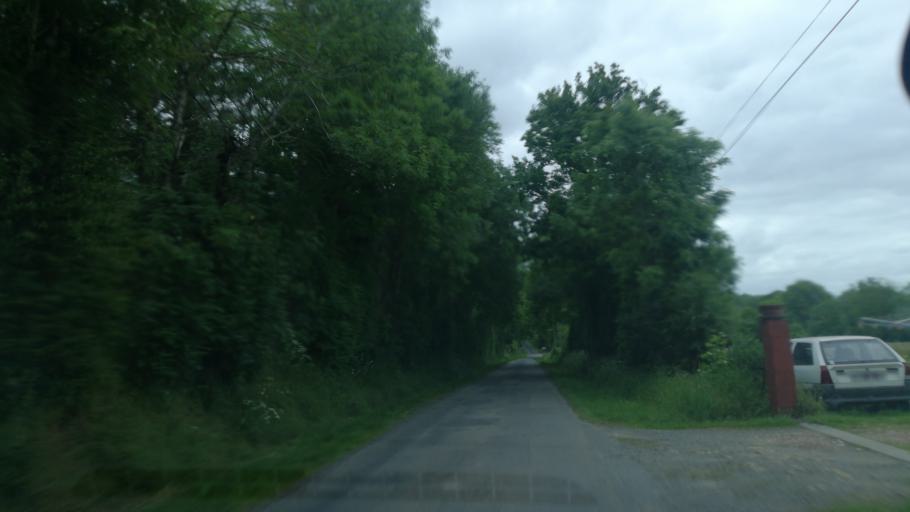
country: FR
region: Poitou-Charentes
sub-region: Departement des Deux-Sevres
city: Boisme
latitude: 46.7931
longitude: -0.4098
